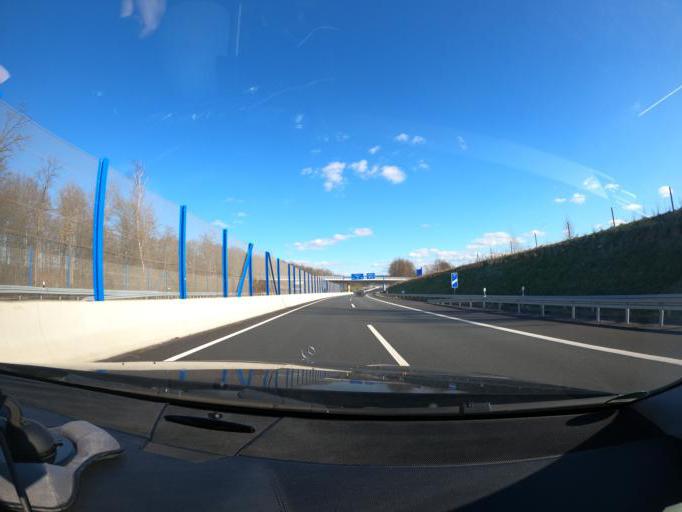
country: DE
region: North Rhine-Westphalia
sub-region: Regierungsbezirk Arnsberg
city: Bochum
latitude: 51.4637
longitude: 7.2748
